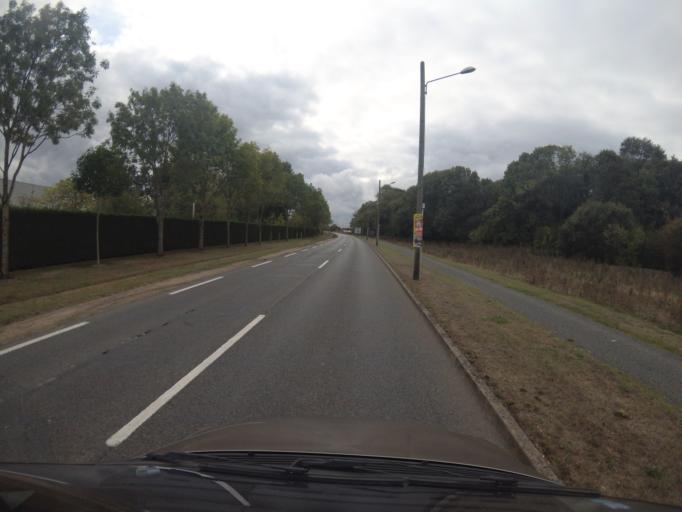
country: FR
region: Ile-de-France
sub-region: Departement de Seine-et-Marne
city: Chessy
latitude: 48.8697
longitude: 2.7659
